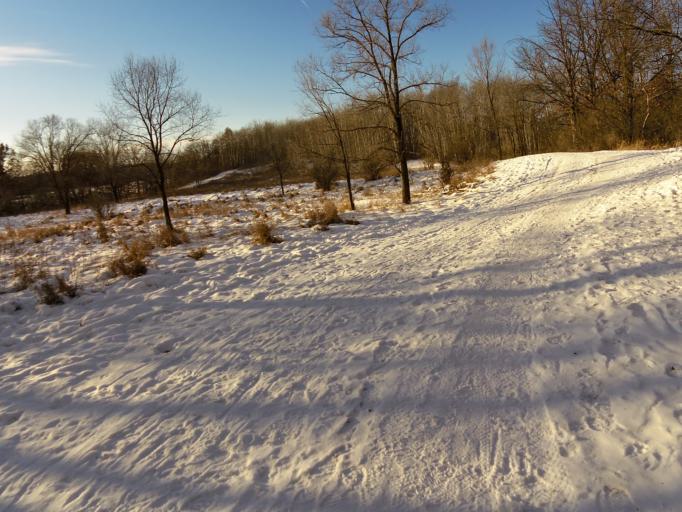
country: US
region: Minnesota
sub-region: Washington County
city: Lake Elmo
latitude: 44.9771
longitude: -92.9053
